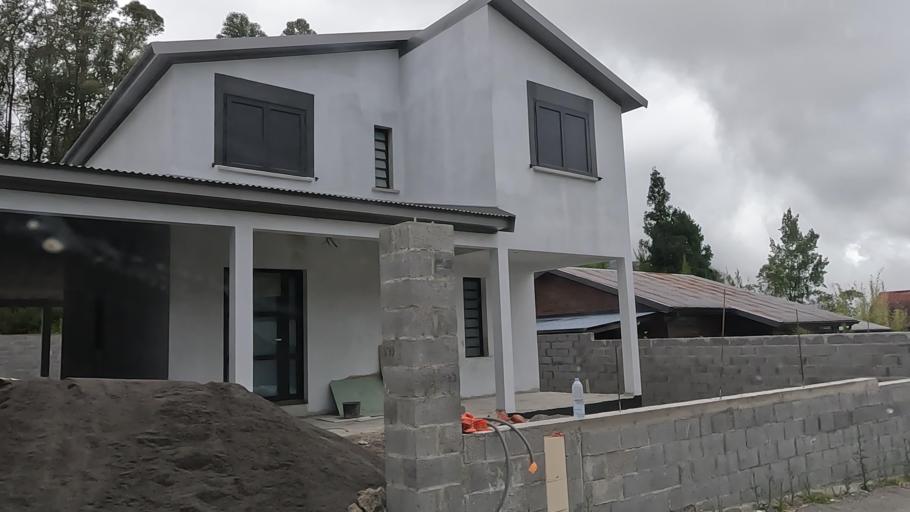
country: RE
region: Reunion
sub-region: Reunion
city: Saint-Benoit
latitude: -21.1400
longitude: 55.6254
